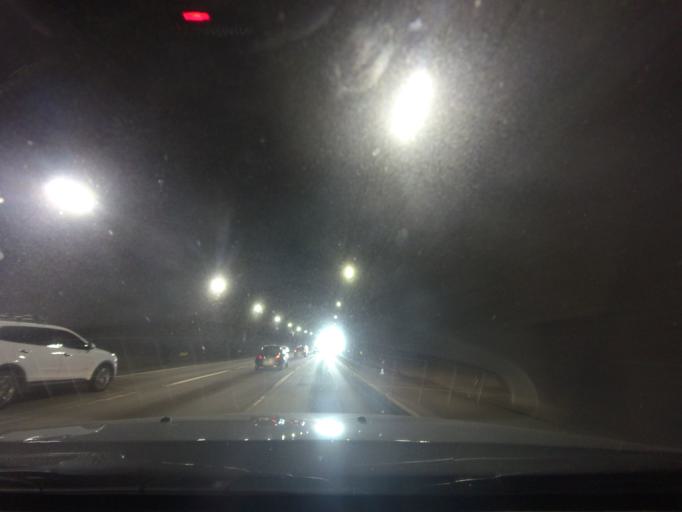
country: BR
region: Sao Paulo
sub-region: Cubatao
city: Cubatao
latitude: -23.9137
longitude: -46.5201
